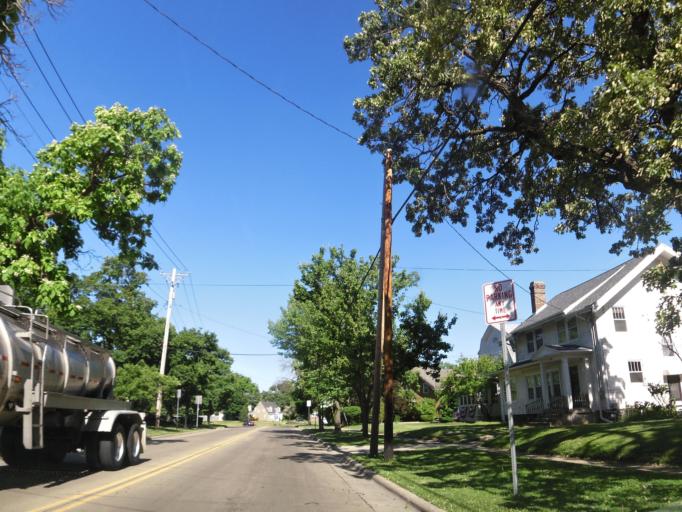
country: US
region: Wisconsin
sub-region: Rock County
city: Beloit
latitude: 42.5109
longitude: -89.0146
